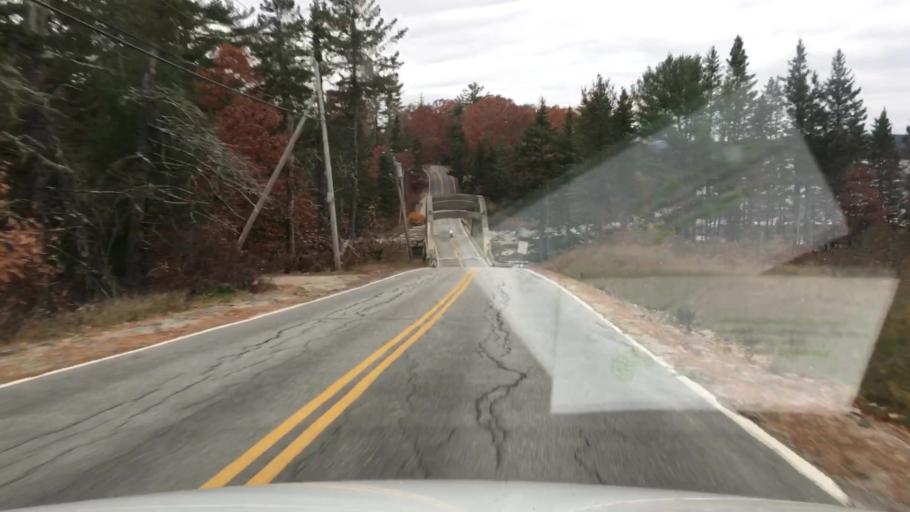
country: US
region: Maine
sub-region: Hancock County
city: Sedgwick
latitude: 44.3730
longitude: -68.5588
